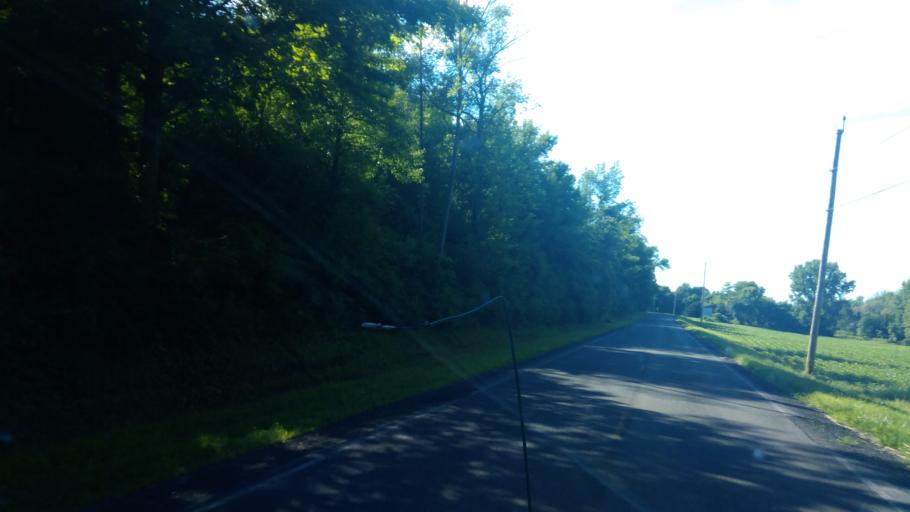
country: US
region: New York
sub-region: Wayne County
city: Lyons
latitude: 43.0082
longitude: -76.9744
